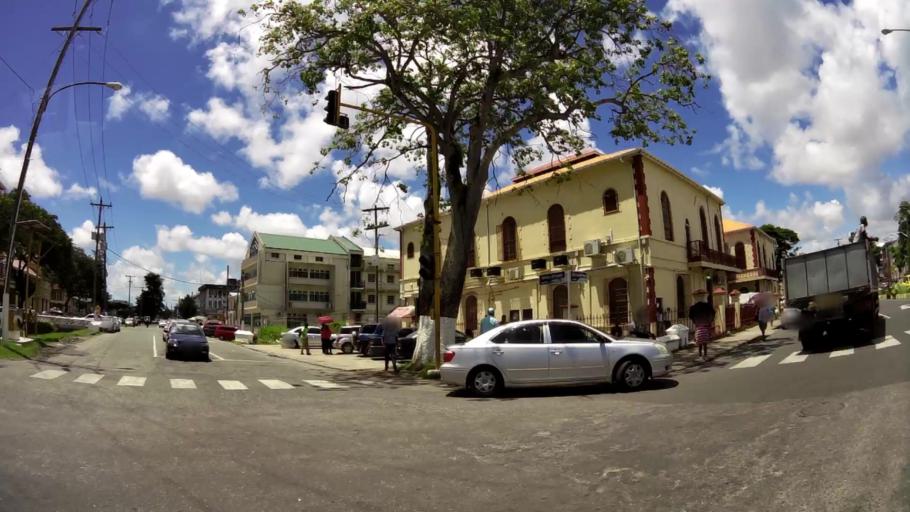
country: GY
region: Demerara-Mahaica
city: Georgetown
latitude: 6.8097
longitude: -58.1658
